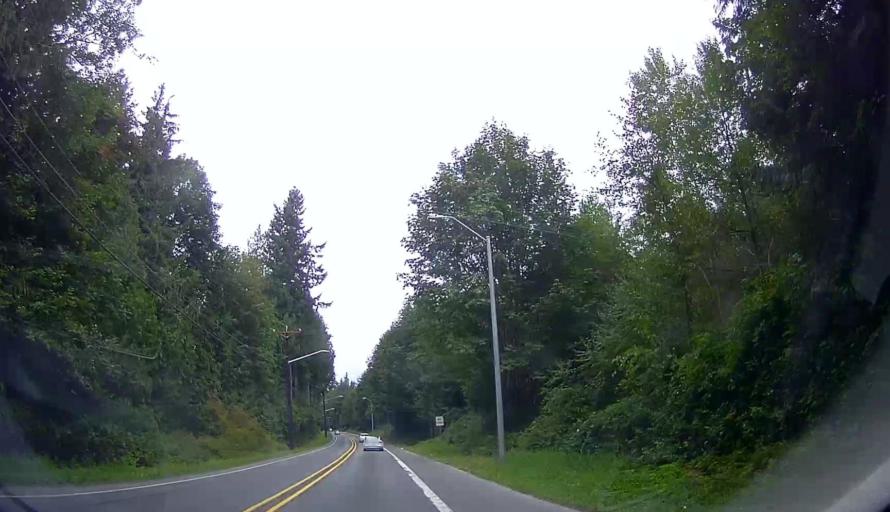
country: US
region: Washington
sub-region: Snohomish County
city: Tulalip
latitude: 48.0476
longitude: -122.2552
